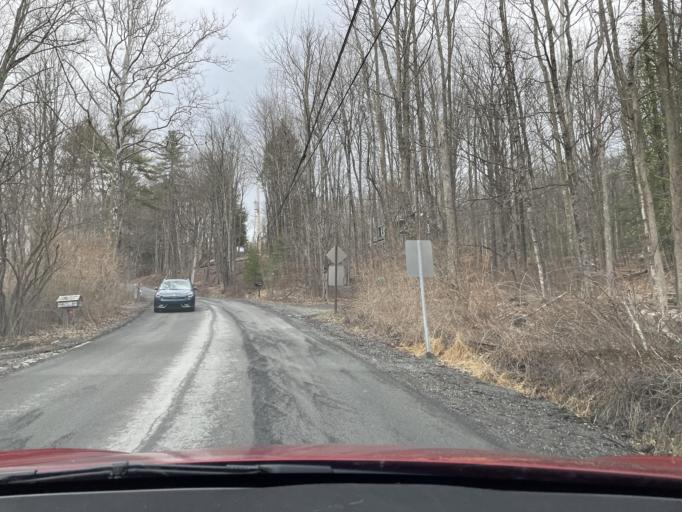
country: US
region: New York
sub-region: Ulster County
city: Woodstock
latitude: 42.0667
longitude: -74.1590
